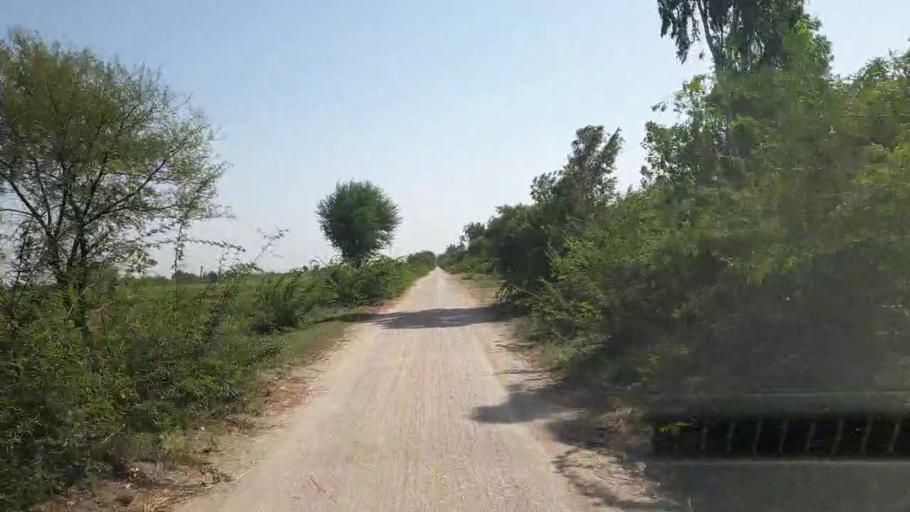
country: PK
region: Sindh
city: Tando Bago
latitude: 24.6540
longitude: 68.9816
